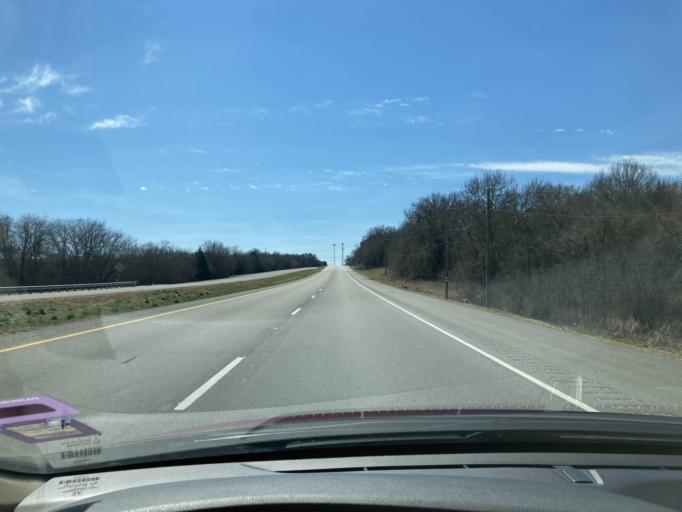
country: US
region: Texas
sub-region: Navarro County
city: Corsicana
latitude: 32.1449
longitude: -96.4681
